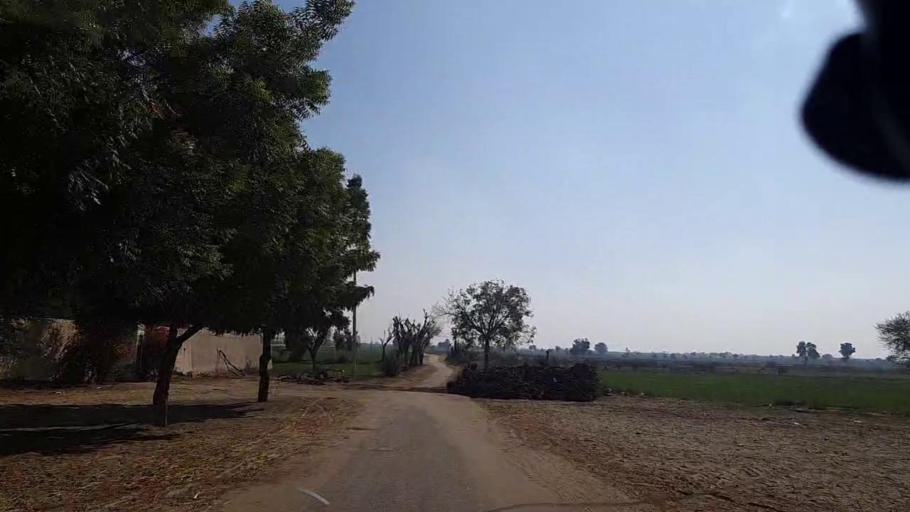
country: PK
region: Sindh
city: Khanpur
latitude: 27.7277
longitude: 69.4398
